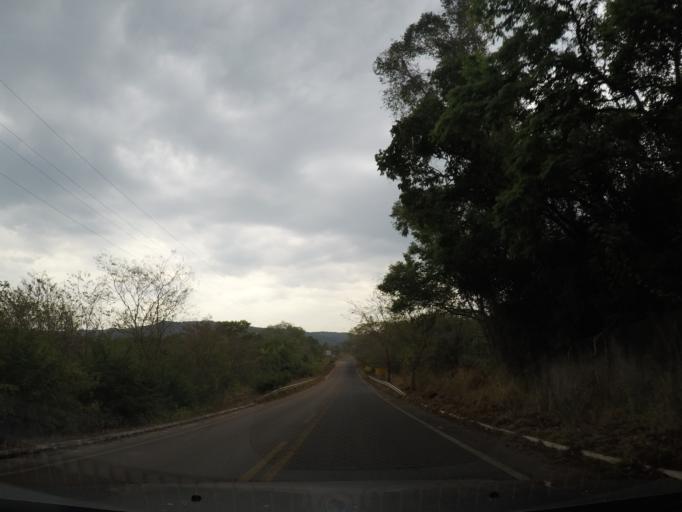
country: BR
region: Goias
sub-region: Pirenopolis
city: Pirenopolis
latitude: -15.8488
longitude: -48.9281
